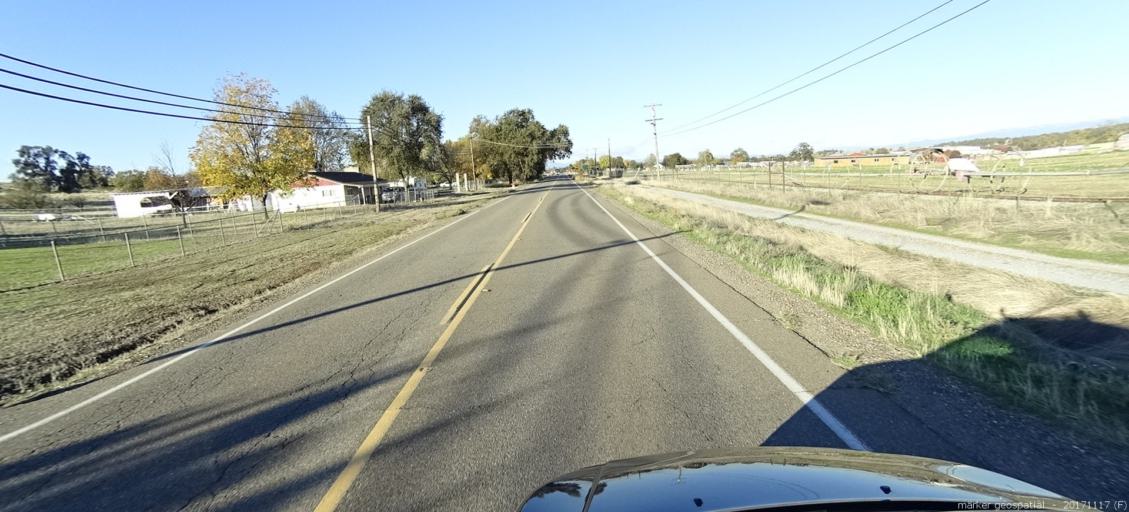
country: US
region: California
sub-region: Shasta County
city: Anderson
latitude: 40.4725
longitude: -122.2421
